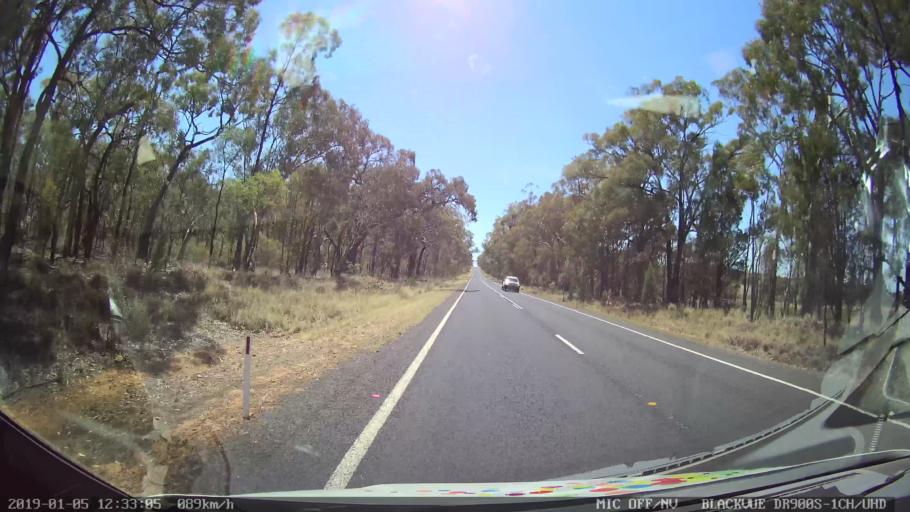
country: AU
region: New South Wales
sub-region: Warrumbungle Shire
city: Coonabarabran
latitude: -31.2156
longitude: 149.3894
